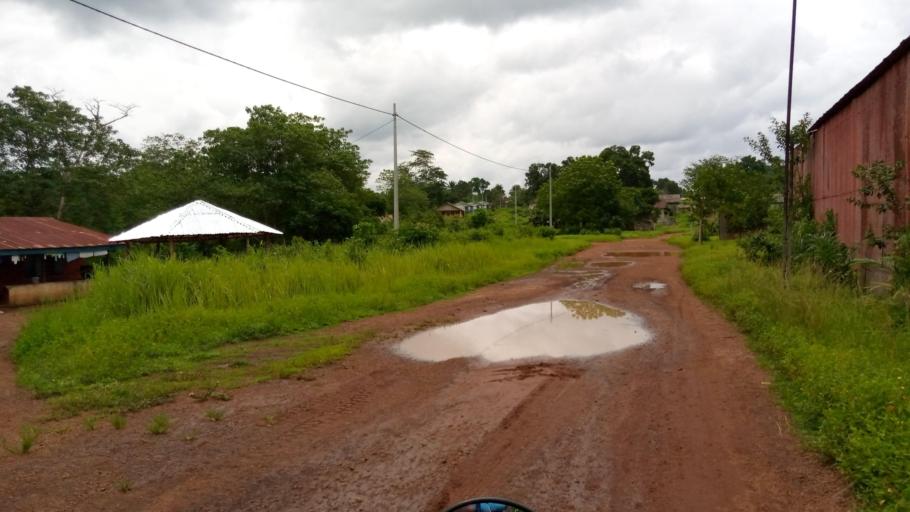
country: SL
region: Southern Province
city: Rotifunk
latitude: 8.1909
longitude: -12.5694
